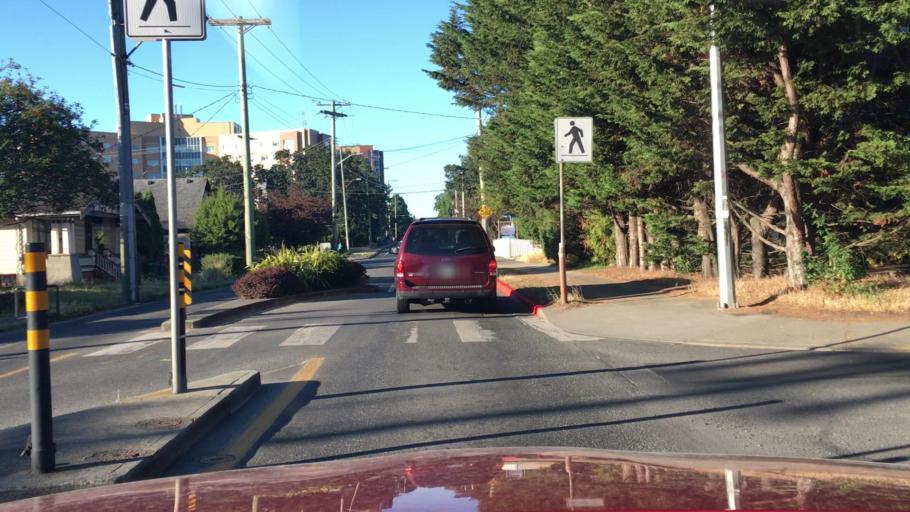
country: CA
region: British Columbia
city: Oak Bay
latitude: 48.4359
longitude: -123.3288
